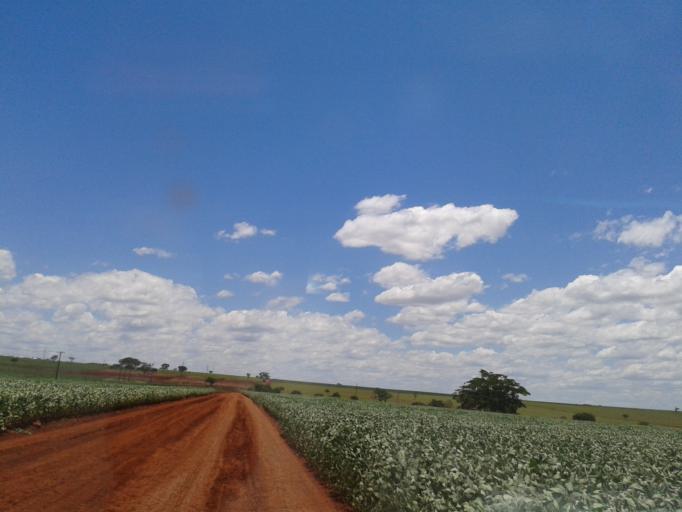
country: BR
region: Minas Gerais
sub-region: Centralina
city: Centralina
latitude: -18.6986
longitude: -49.2178
